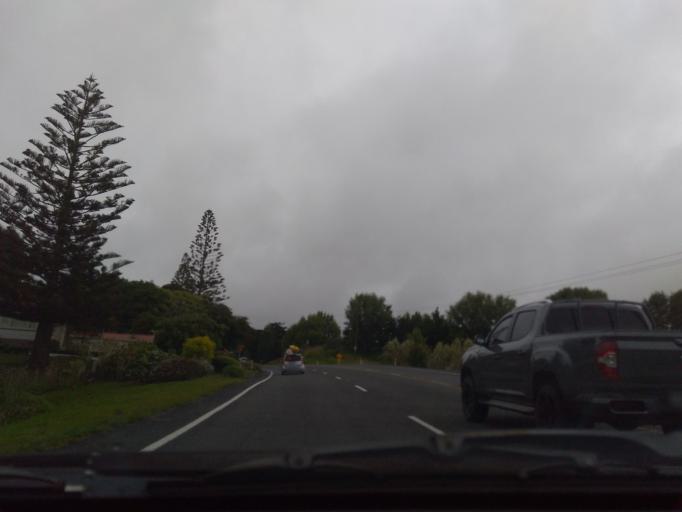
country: NZ
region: Auckland
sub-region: Auckland
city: Wellsford
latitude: -36.1506
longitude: 174.4390
